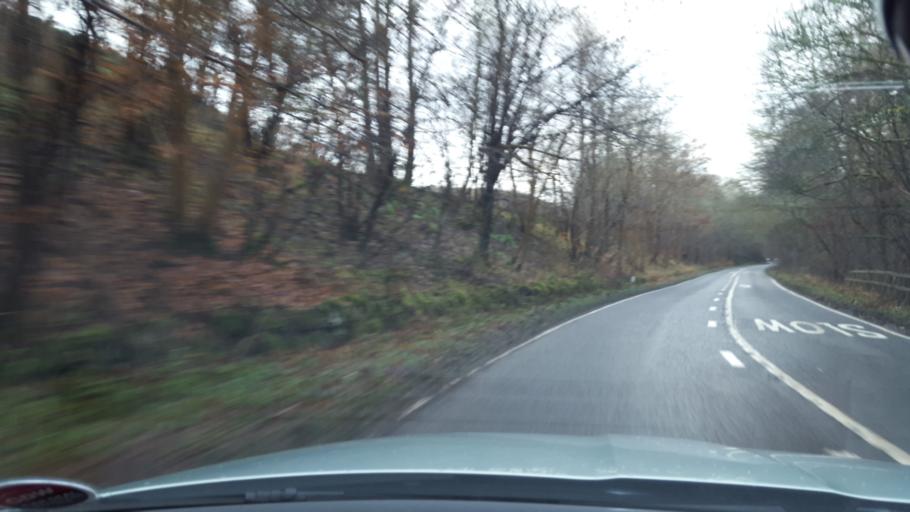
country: GB
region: Scotland
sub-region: Perth and Kinross
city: Bridge of Earn
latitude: 56.3020
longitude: -3.3693
